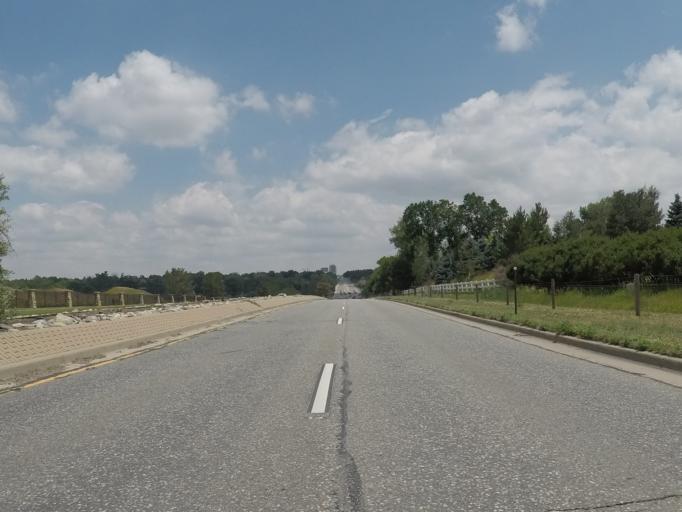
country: US
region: Colorado
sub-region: Arapahoe County
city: Greenwood Village
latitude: 39.6242
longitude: -104.9474
